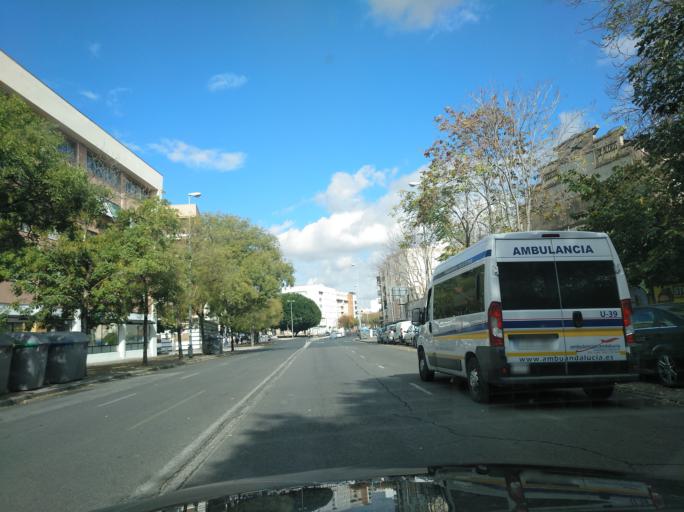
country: ES
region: Andalusia
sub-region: Provincia de Sevilla
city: Sevilla
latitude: 37.3863
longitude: -5.9833
